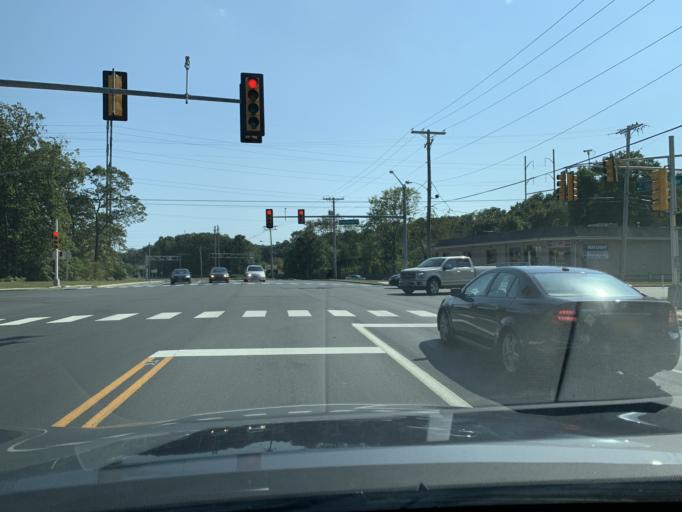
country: US
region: New Jersey
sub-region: Monmouth County
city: Tinton Falls
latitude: 40.2869
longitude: -74.0951
